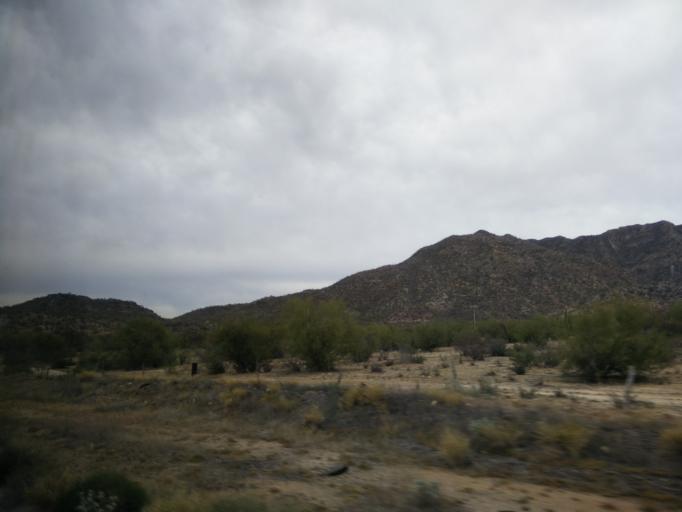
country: MX
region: Sonora
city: Hermosillo
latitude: 28.9736
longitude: -110.9639
